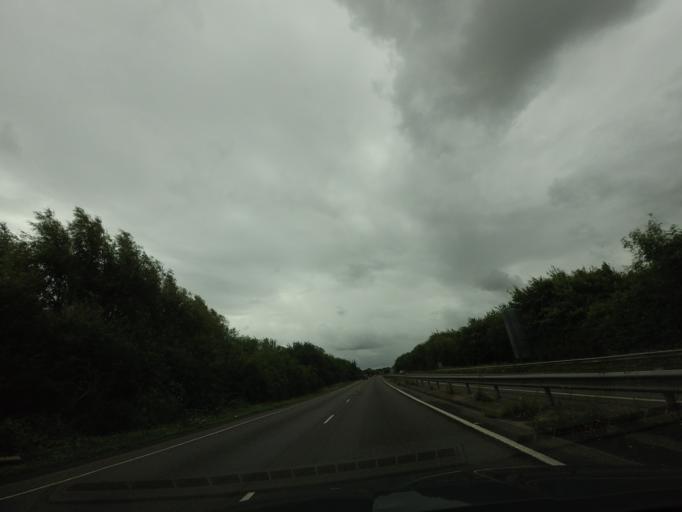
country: GB
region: England
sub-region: Kent
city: East Peckham
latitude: 51.2233
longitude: 0.3979
